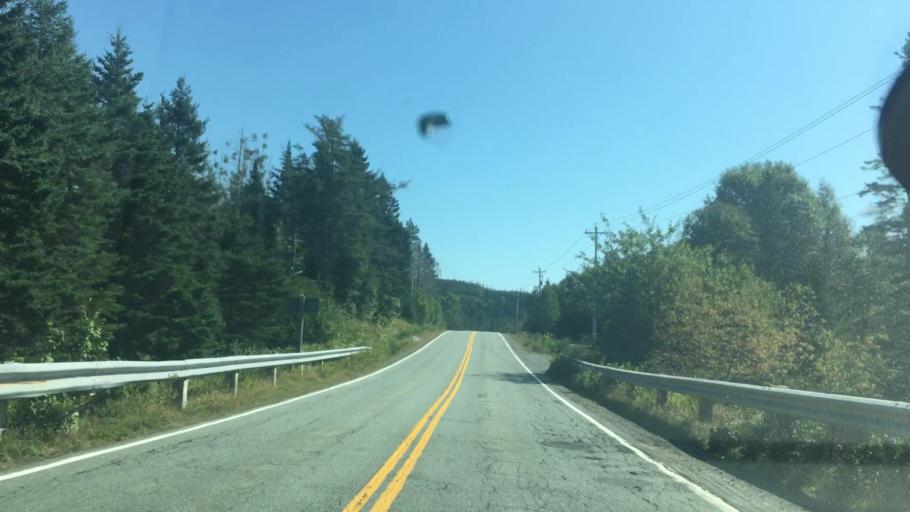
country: CA
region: Nova Scotia
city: Antigonish
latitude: 45.0128
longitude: -62.0967
